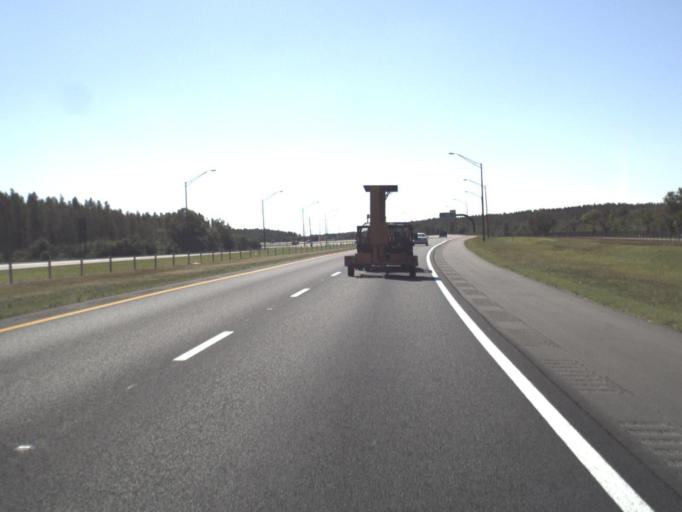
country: US
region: Florida
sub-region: Hillsborough County
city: Cheval
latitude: 28.1659
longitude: -82.5363
